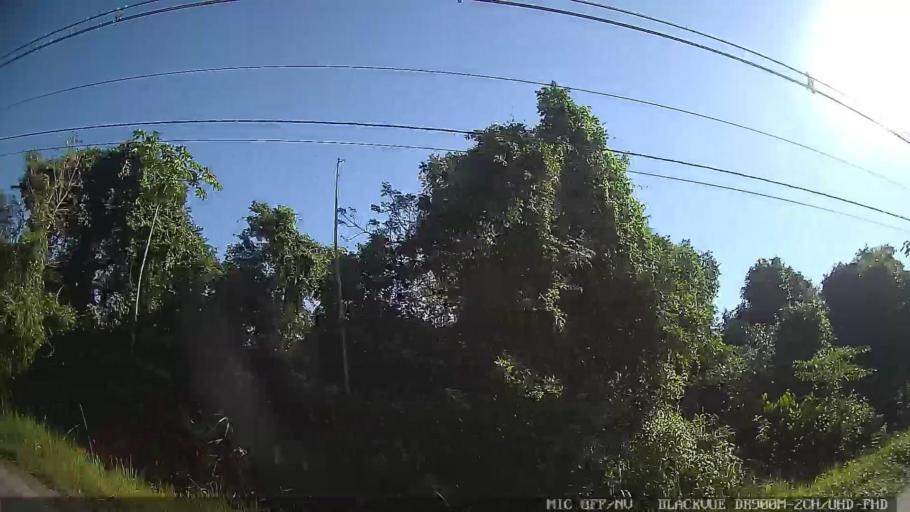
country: BR
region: Sao Paulo
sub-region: Santos
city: Santos
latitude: -23.9043
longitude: -46.3086
